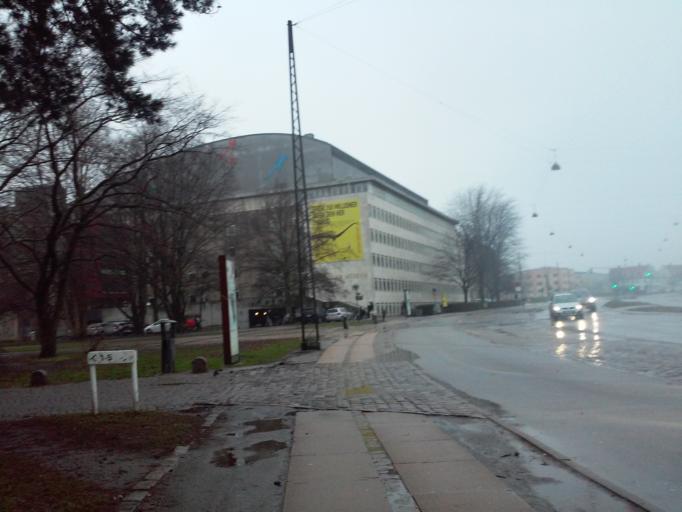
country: DK
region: Capital Region
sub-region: Kobenhavn
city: Copenhagen
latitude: 55.7024
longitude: 12.5608
